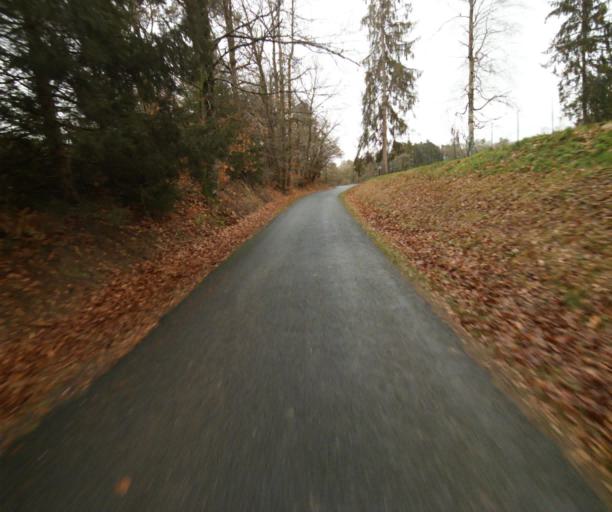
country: FR
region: Limousin
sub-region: Departement de la Correze
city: Saint-Mexant
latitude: 45.2954
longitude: 1.6328
